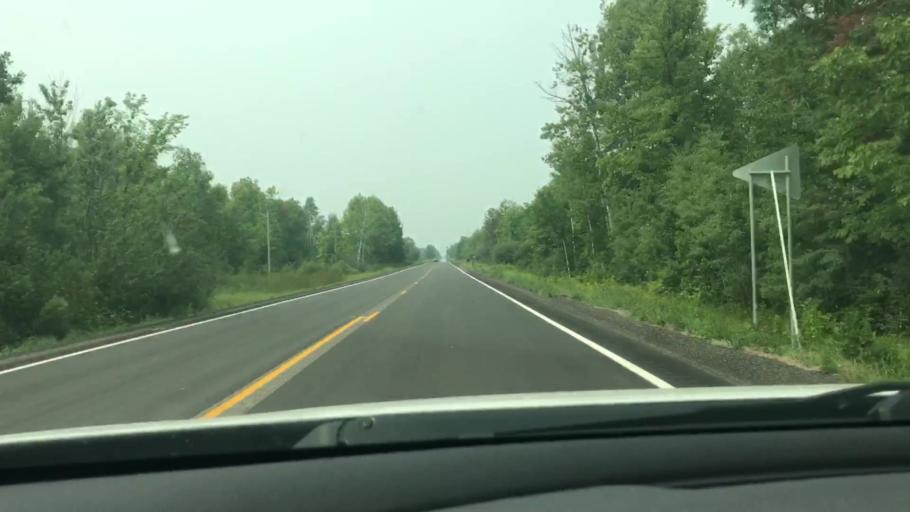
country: US
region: Minnesota
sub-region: Itasca County
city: Cohasset
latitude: 47.3610
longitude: -93.8641
